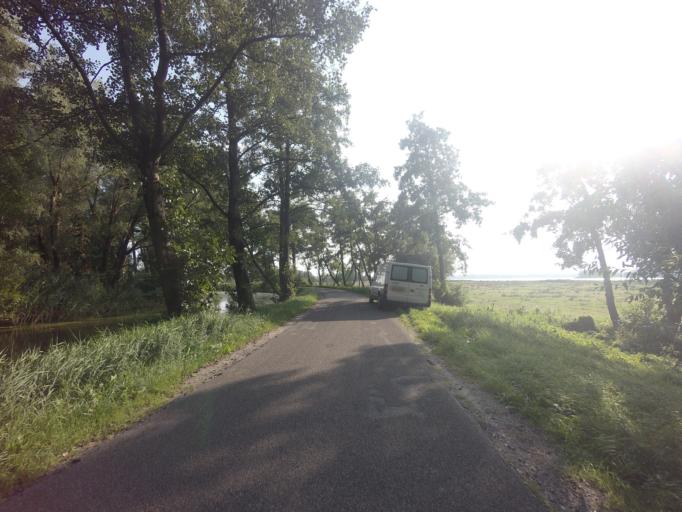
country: NL
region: Groningen
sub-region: Gemeente Haren
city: Haren
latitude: 53.1758
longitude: 6.5785
